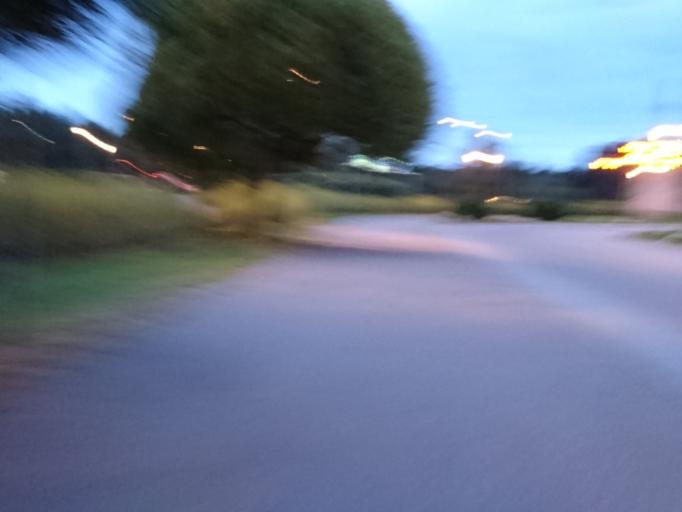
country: SE
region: Stockholm
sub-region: Stockholms Kommun
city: Arsta
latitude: 59.2789
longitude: 18.0199
